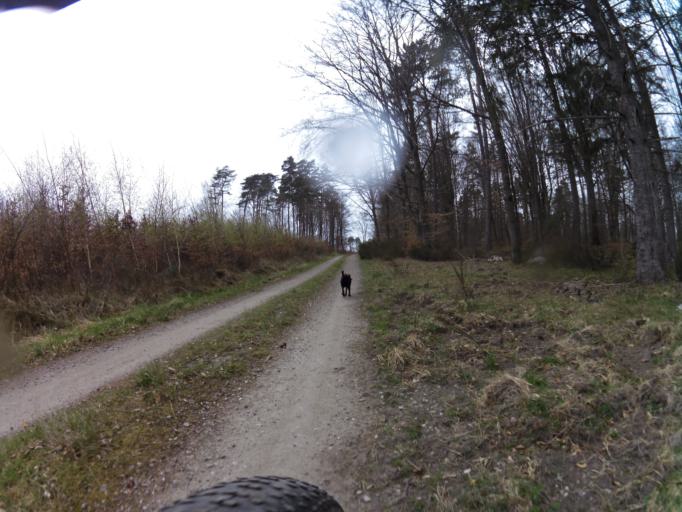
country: PL
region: West Pomeranian Voivodeship
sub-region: Powiat koszalinski
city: Polanow
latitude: 54.0727
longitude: 16.6216
